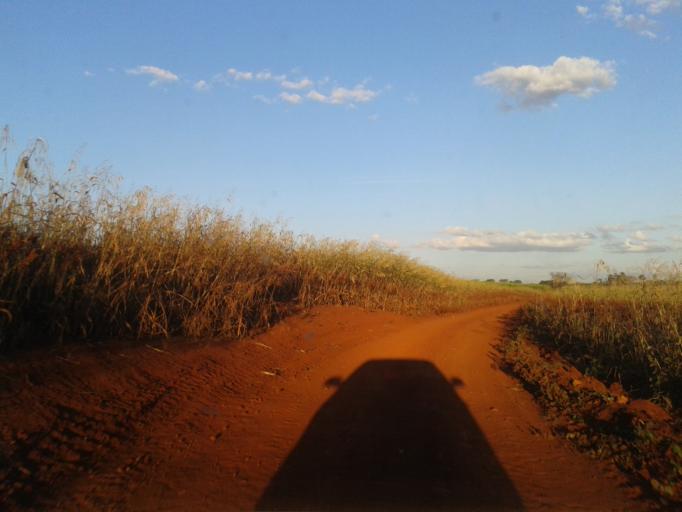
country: BR
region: Minas Gerais
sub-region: Centralina
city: Centralina
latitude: -18.6049
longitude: -49.3021
